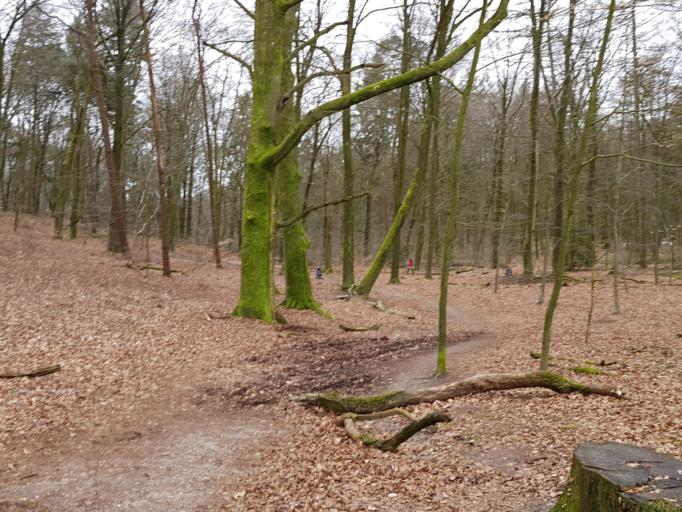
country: NL
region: Gelderland
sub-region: Gemeente Renkum
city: Oosterbeek
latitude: 51.9850
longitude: 5.8307
